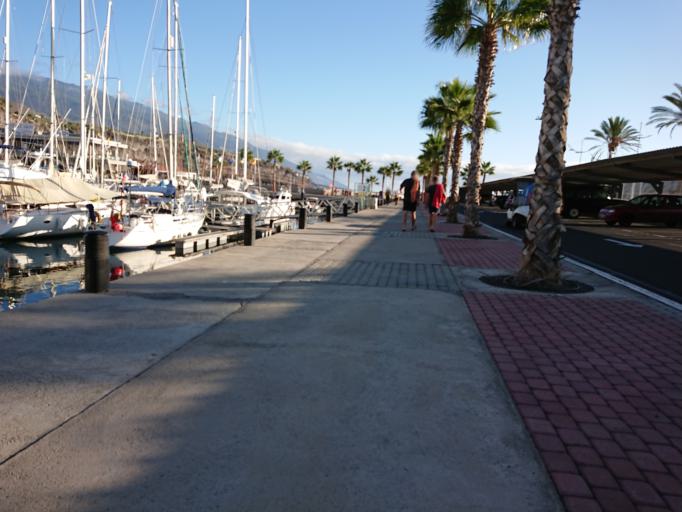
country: ES
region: Canary Islands
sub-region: Provincia de Santa Cruz de Tenerife
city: Tazacorte
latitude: 28.6443
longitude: -17.9441
